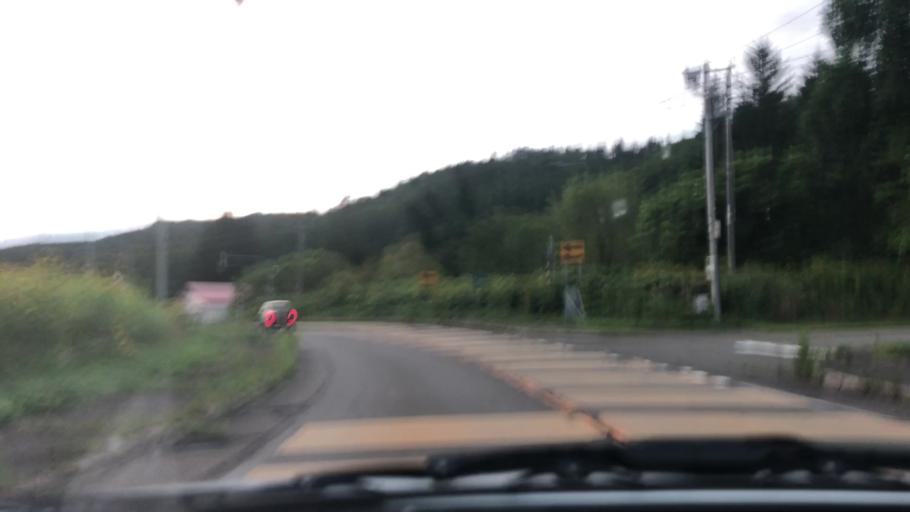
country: JP
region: Hokkaido
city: Iwamizawa
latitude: 42.9311
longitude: 142.0942
